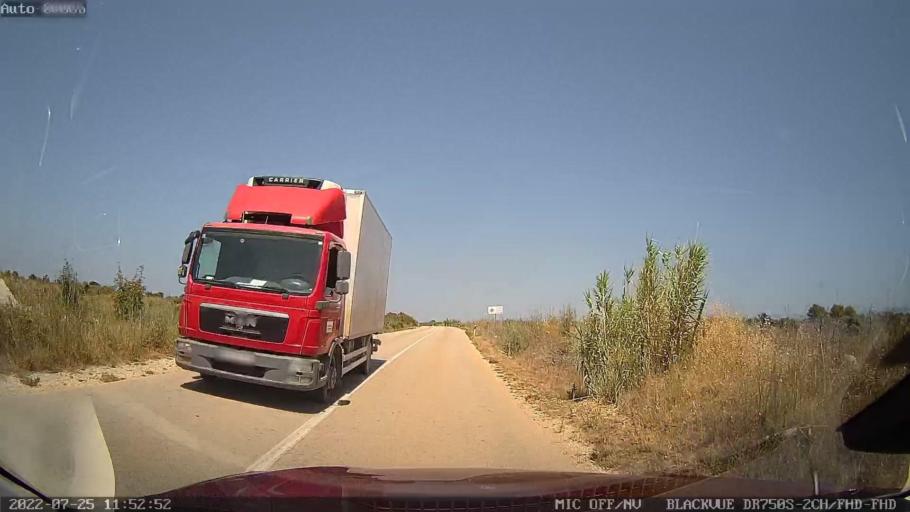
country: HR
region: Zadarska
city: Vrsi
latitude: 44.2513
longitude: 15.2391
